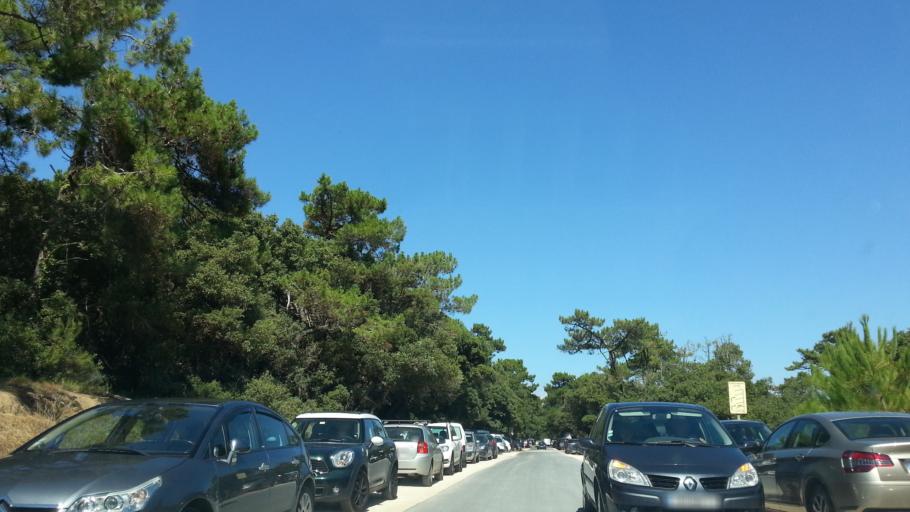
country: FR
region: Poitou-Charentes
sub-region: Departement de la Charente-Maritime
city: Dolus-d'Oleron
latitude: 45.8778
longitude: -1.2610
